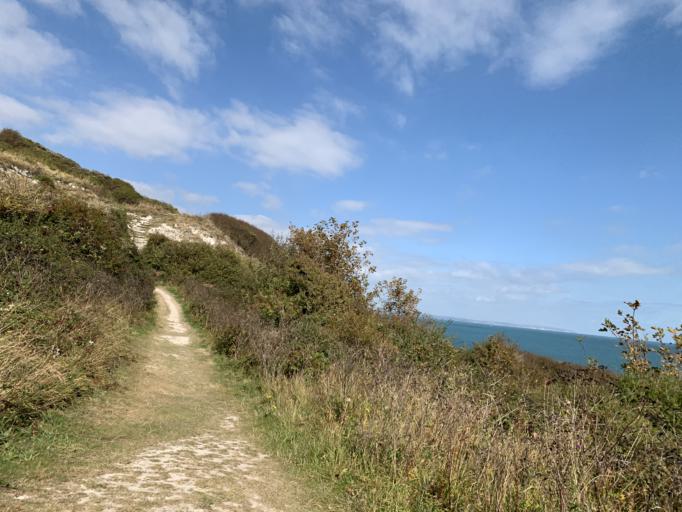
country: GB
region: England
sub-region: East Sussex
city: Eastbourne
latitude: 50.7429
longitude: 0.2625
